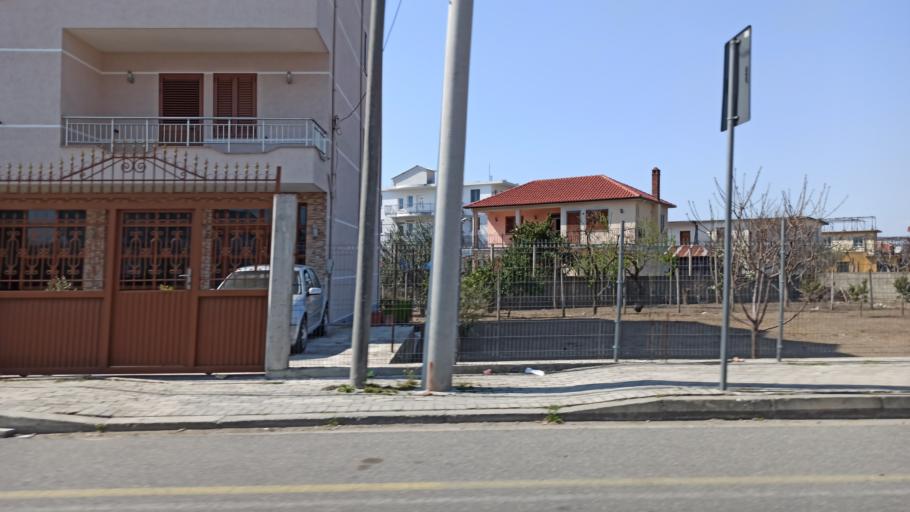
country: AL
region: Shkoder
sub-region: Rrethi i Malesia e Madhe
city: Kuc
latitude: 42.0557
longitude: 19.5238
